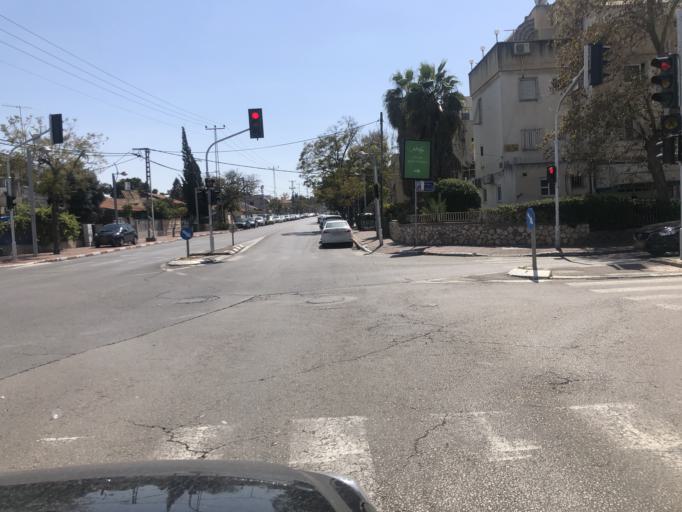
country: IL
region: Tel Aviv
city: Holon
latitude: 32.0105
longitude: 34.7648
